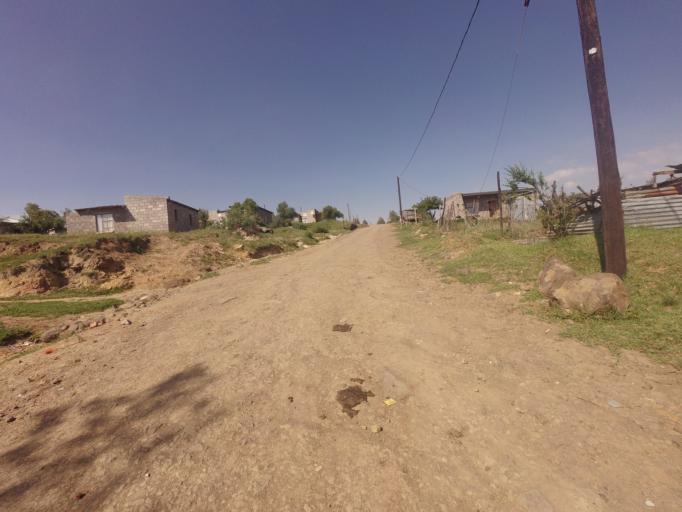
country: LS
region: Berea
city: Teyateyaneng
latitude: -29.1452
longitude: 27.7567
